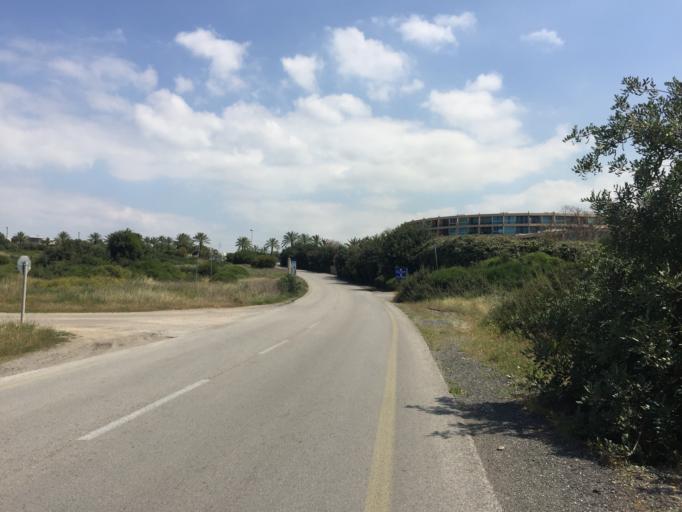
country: IL
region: Haifa
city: Qesarya
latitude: 32.4908
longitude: 34.9008
